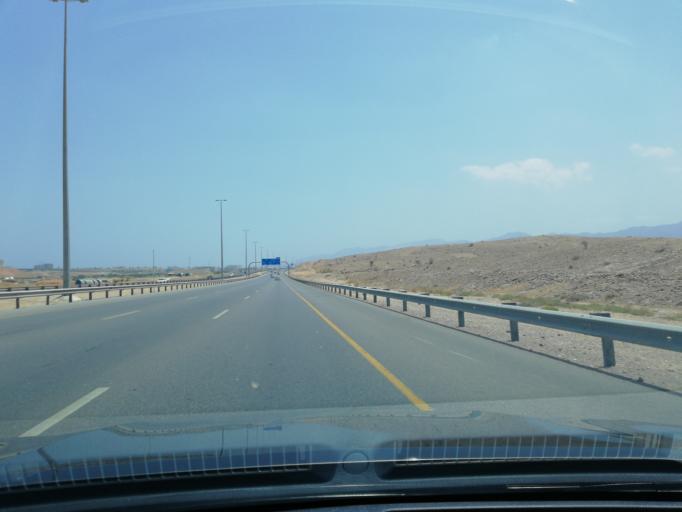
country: OM
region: Muhafazat Masqat
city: Bawshar
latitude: 23.5574
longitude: 58.3157
